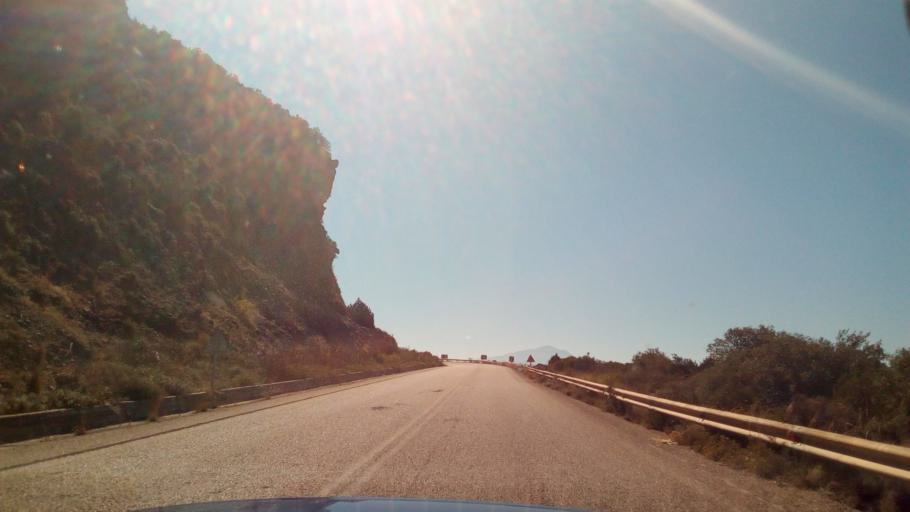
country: GR
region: West Greece
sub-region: Nomos Achaias
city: Selianitika
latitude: 38.3731
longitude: 22.0973
